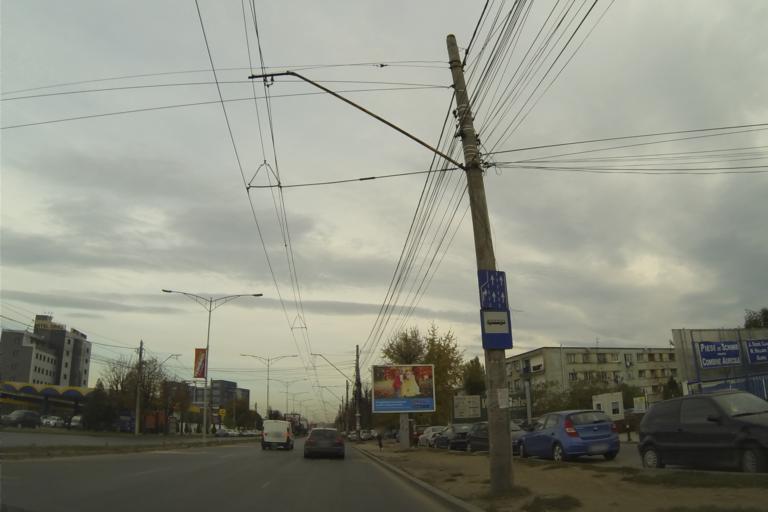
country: RO
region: Ilfov
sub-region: Comuna Chiajna
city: Rosu
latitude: 44.4345
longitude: 25.9874
